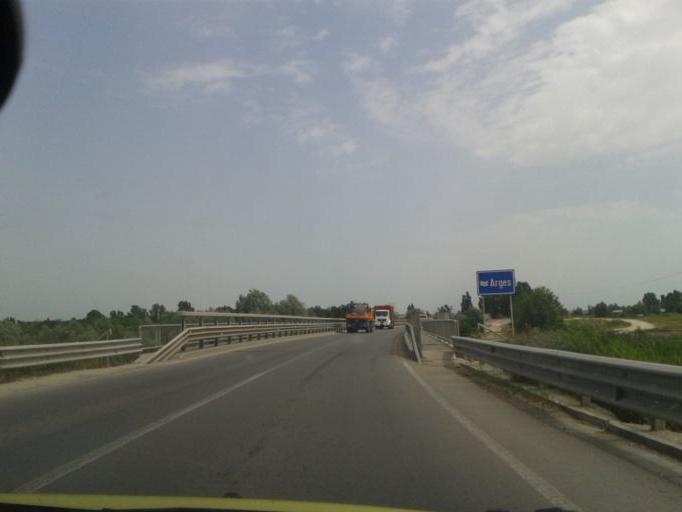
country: RO
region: Dambovita
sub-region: Comuna Petresti
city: Ionesti
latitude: 44.6813
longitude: 25.3111
